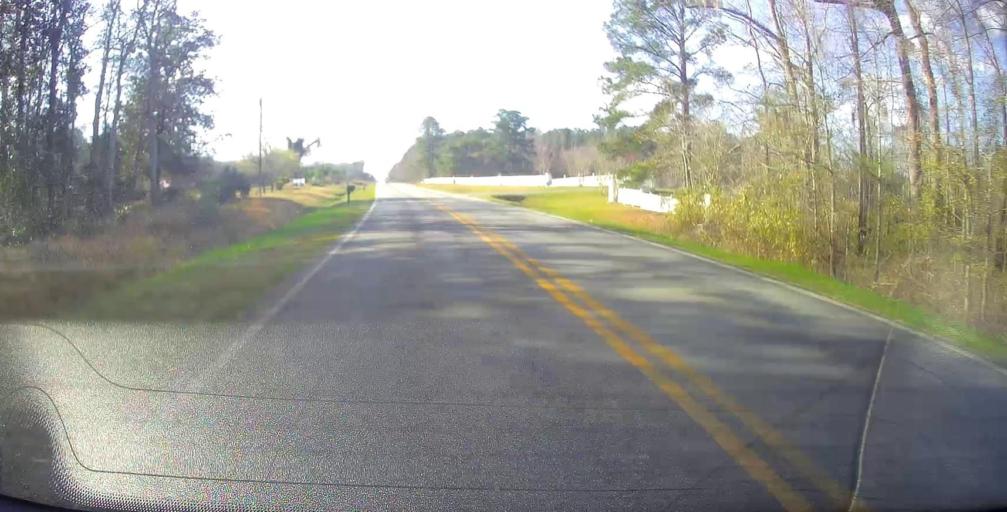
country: US
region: Georgia
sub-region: Laurens County
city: Dublin
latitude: 32.5565
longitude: -82.9981
